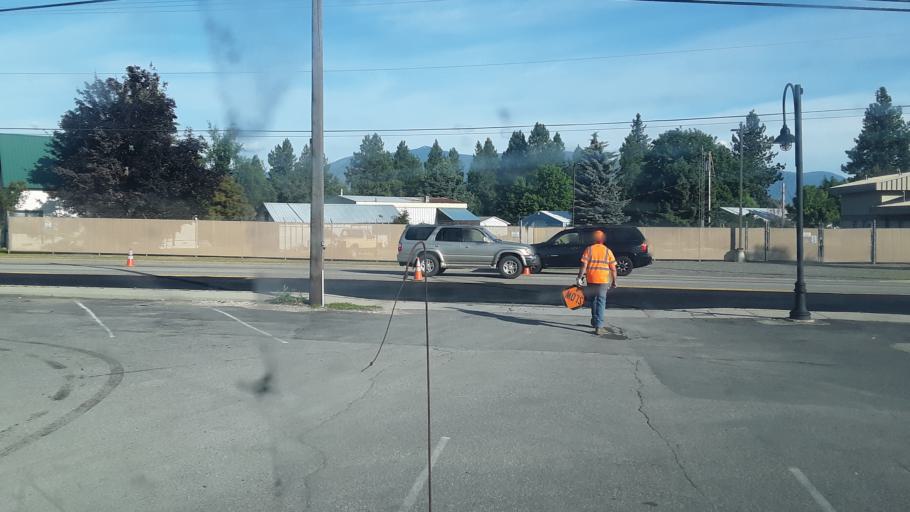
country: US
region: Idaho
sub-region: Boundary County
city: Bonners Ferry
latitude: 48.6796
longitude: -116.3274
